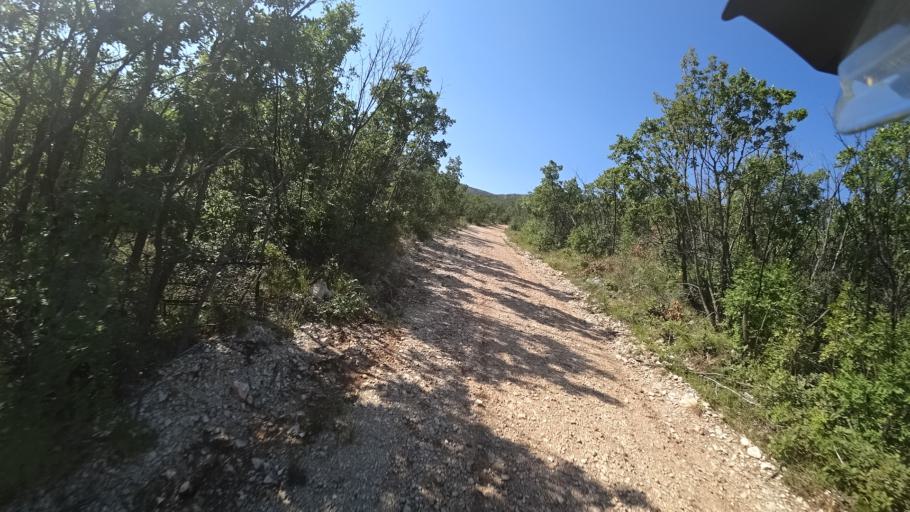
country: HR
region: Sibensko-Kniniska
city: Knin
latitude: 43.9595
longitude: 16.1633
